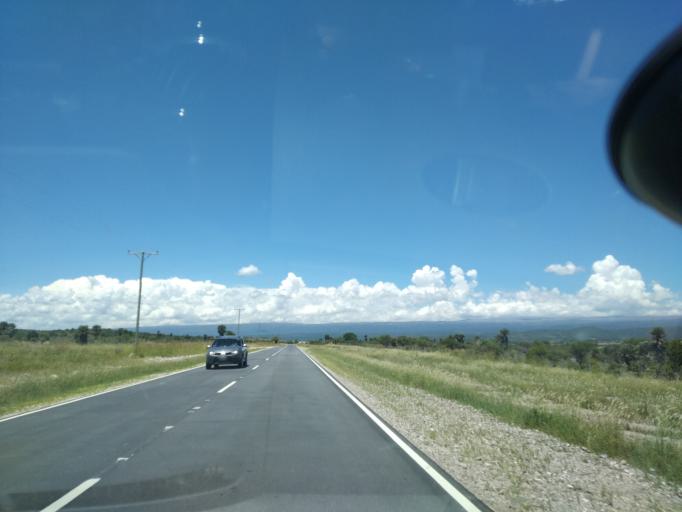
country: AR
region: Cordoba
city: Salsacate
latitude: -31.3567
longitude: -65.1559
